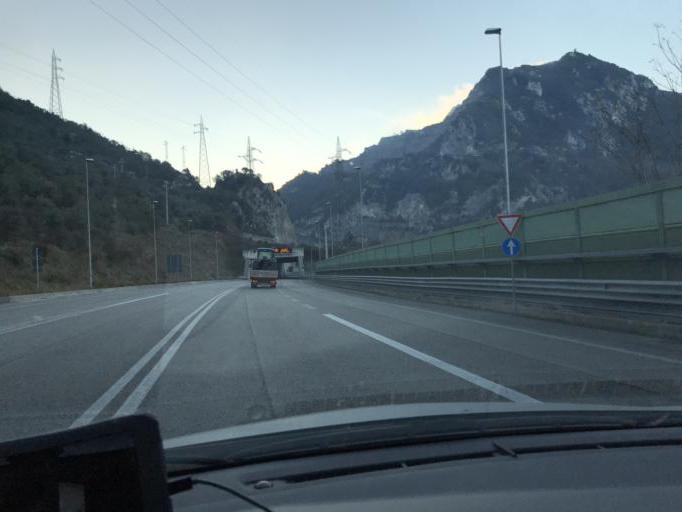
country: IT
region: Umbria
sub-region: Provincia di Terni
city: Terni
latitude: 42.5556
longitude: 12.6960
